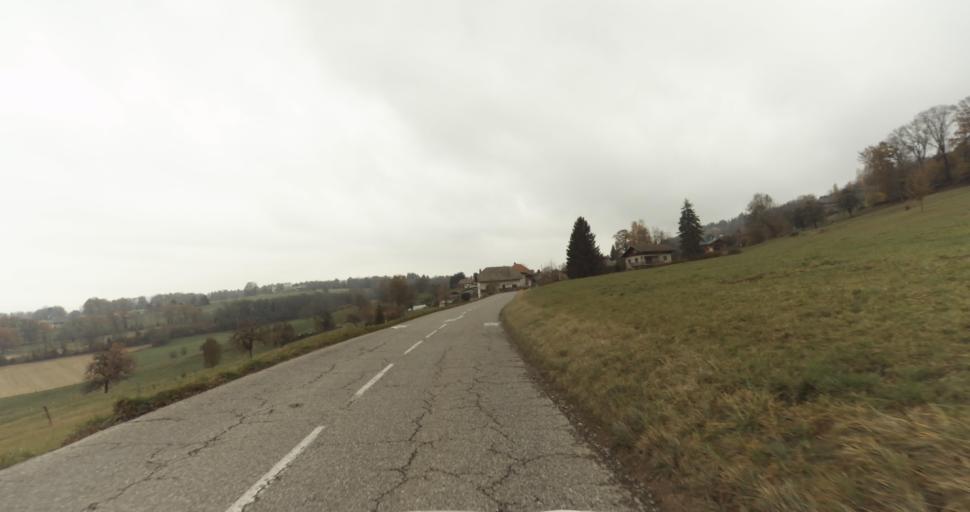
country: FR
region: Rhone-Alpes
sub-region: Departement de la Haute-Savoie
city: Gruffy
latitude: 45.7946
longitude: 6.0558
